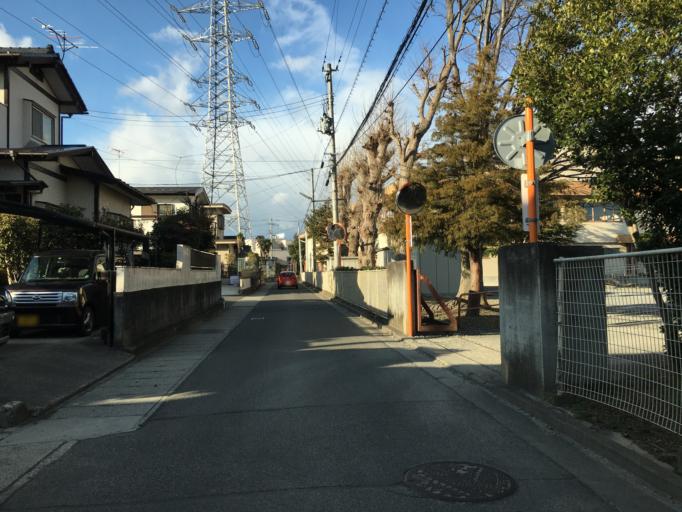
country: JP
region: Fukushima
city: Fukushima-shi
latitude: 37.7792
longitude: 140.4421
